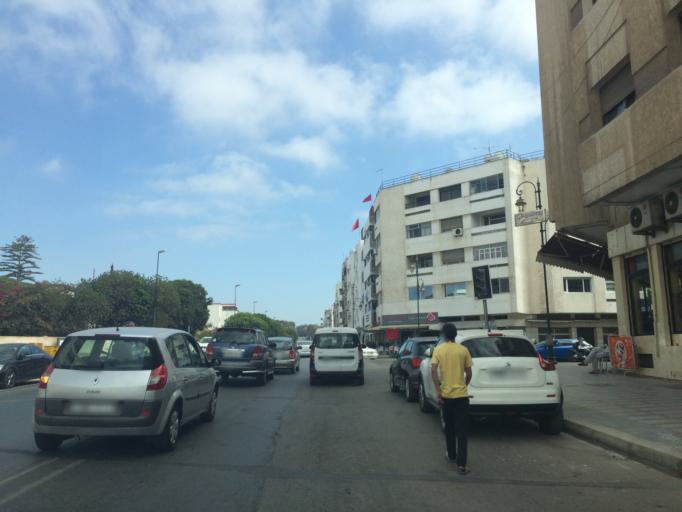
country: MA
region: Rabat-Sale-Zemmour-Zaer
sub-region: Rabat
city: Rabat
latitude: 34.0023
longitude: -6.8458
